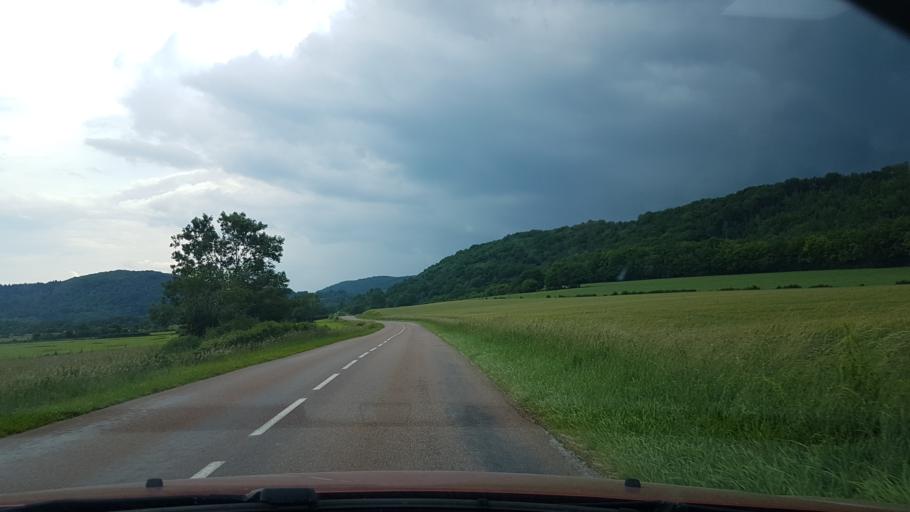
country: FR
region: Franche-Comte
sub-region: Departement du Jura
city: Clairvaux-les-Lacs
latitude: 46.5682
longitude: 5.6753
